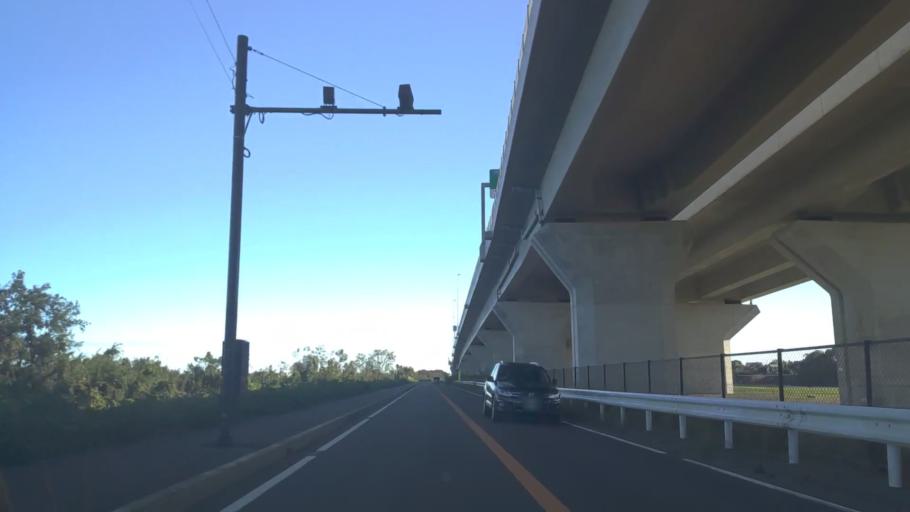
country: JP
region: Kanagawa
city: Zama
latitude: 35.4843
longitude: 139.3714
